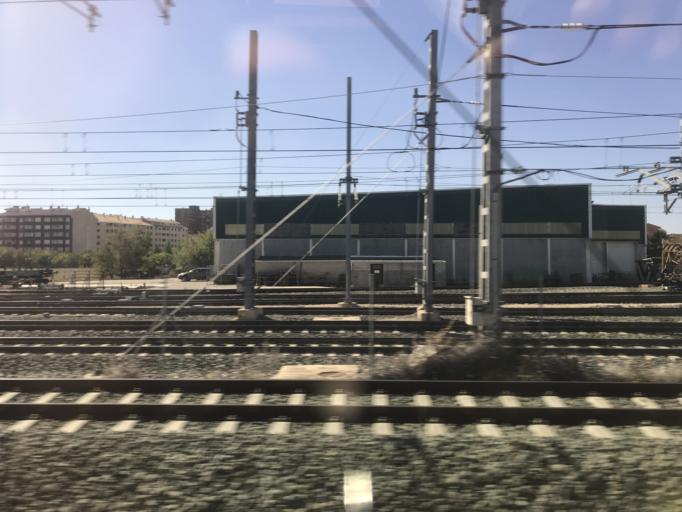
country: ES
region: Castille-La Mancha
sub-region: Provincia de Albacete
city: Albacete
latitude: 39.0040
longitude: -1.8511
